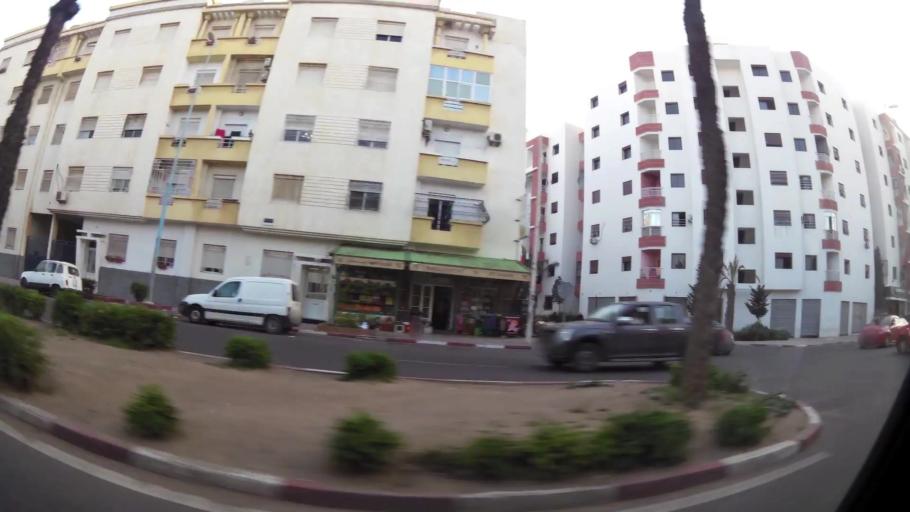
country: MA
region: Oued ed Dahab-Lagouira
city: Dakhla
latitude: 30.4002
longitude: -9.5532
